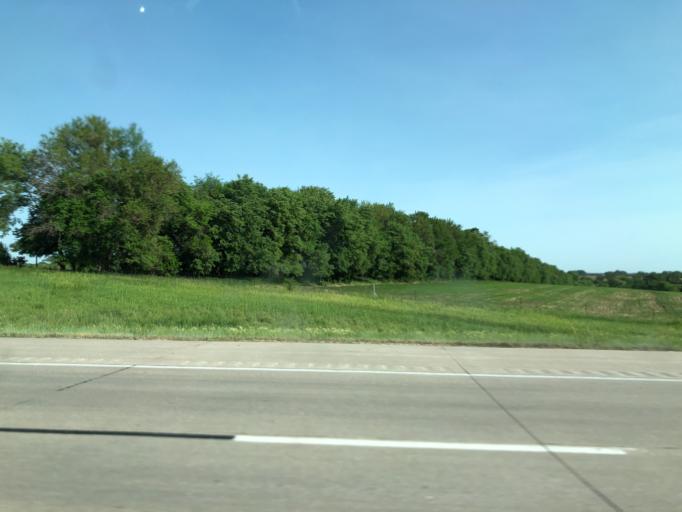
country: US
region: Nebraska
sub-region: Saunders County
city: Ashland
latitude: 40.9919
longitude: -96.3556
